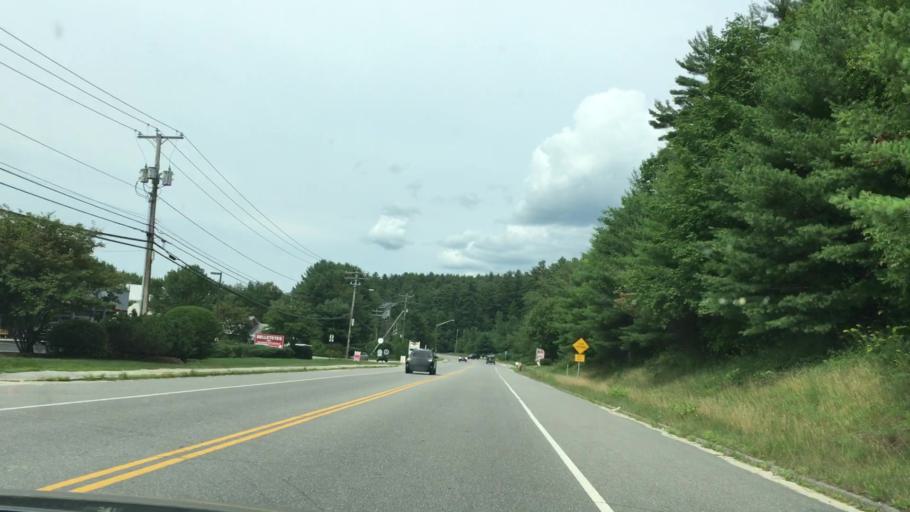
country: US
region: New Hampshire
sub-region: Hillsborough County
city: Peterborough
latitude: 42.8899
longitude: -71.9451
